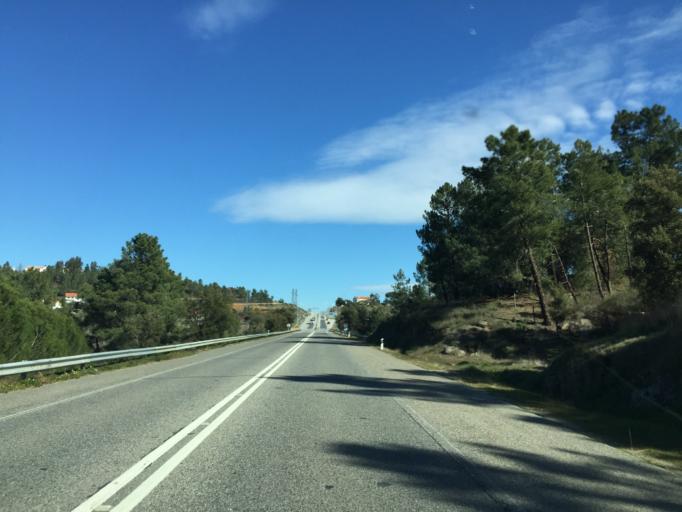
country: PT
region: Castelo Branco
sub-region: Castelo Branco
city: Castelo Branco
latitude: 39.8243
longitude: -7.5152
